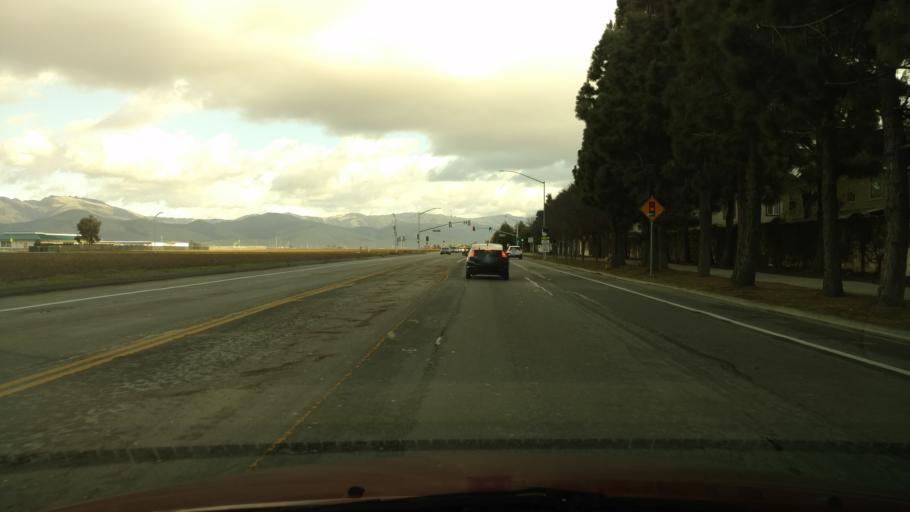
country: US
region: California
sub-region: Monterey County
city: Boronda
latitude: 36.7174
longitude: -121.6458
